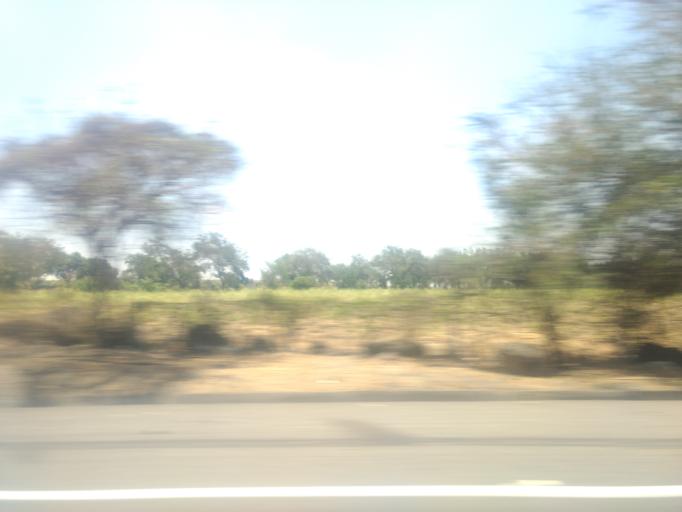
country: MX
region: Colima
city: Cuauhtemoc
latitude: 19.3192
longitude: -103.5914
